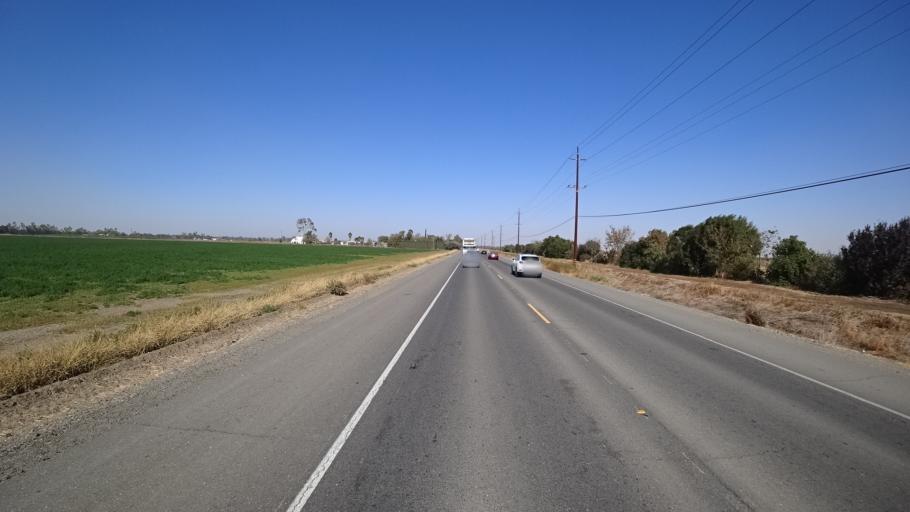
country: US
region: California
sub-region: Yolo County
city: Davis
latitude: 38.6092
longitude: -121.7301
